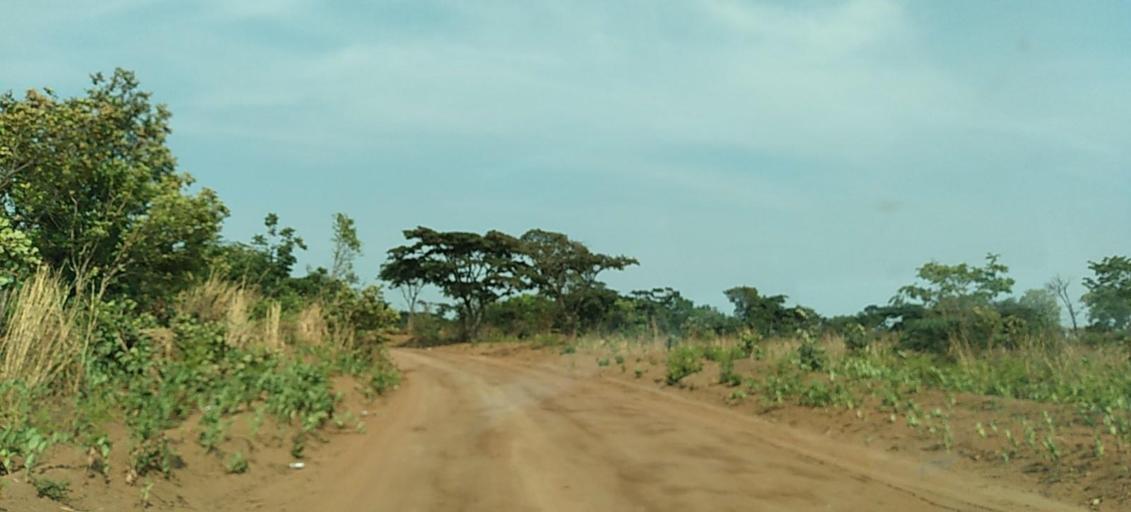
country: ZM
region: Copperbelt
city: Chililabombwe
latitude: -12.2923
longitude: 27.7667
